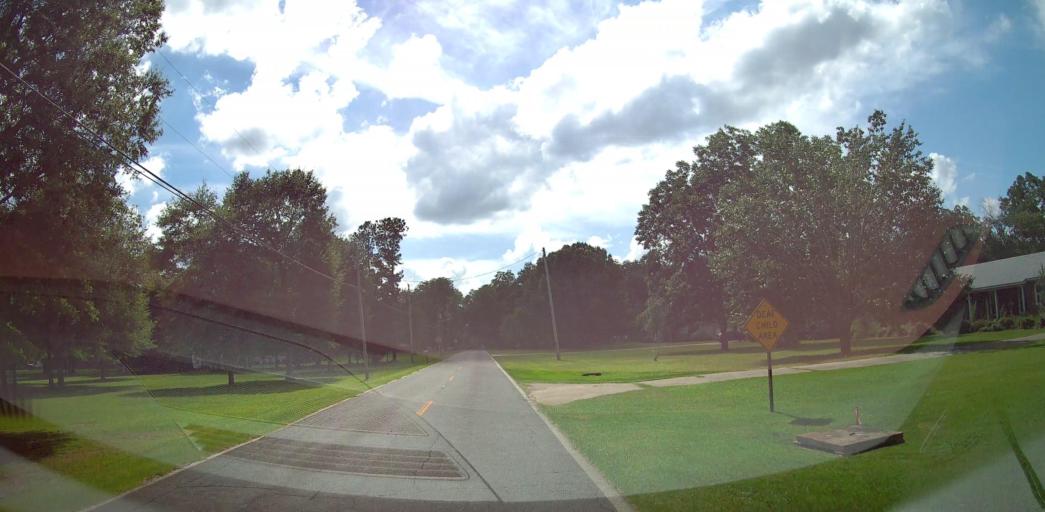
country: US
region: Georgia
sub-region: Houston County
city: Centerville
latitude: 32.7041
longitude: -83.6828
